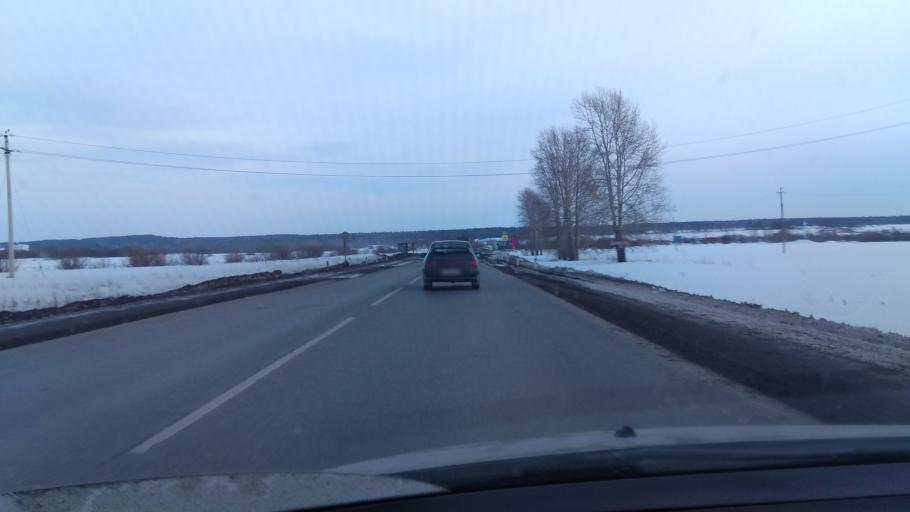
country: RU
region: Perm
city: Kukushtan
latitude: 57.5073
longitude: 56.6480
